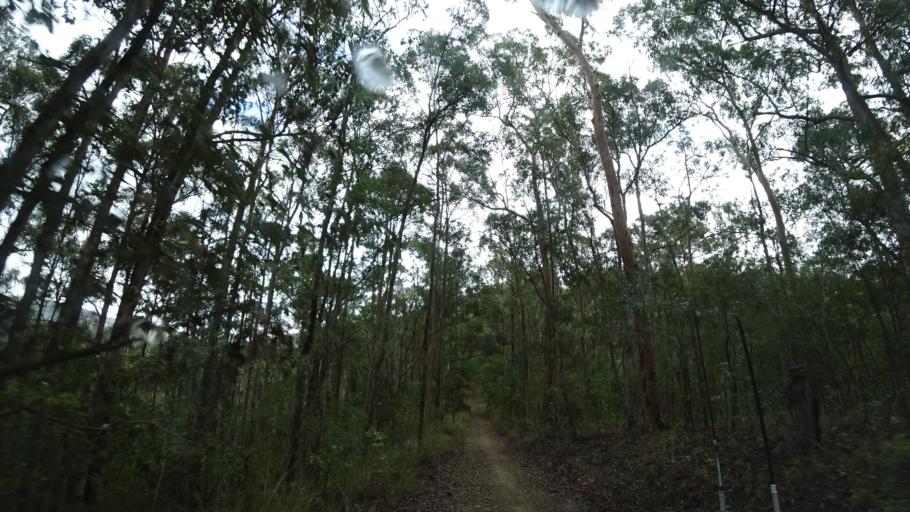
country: AU
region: Queensland
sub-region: Brisbane
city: Pullenvale
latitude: -27.4576
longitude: 152.8275
